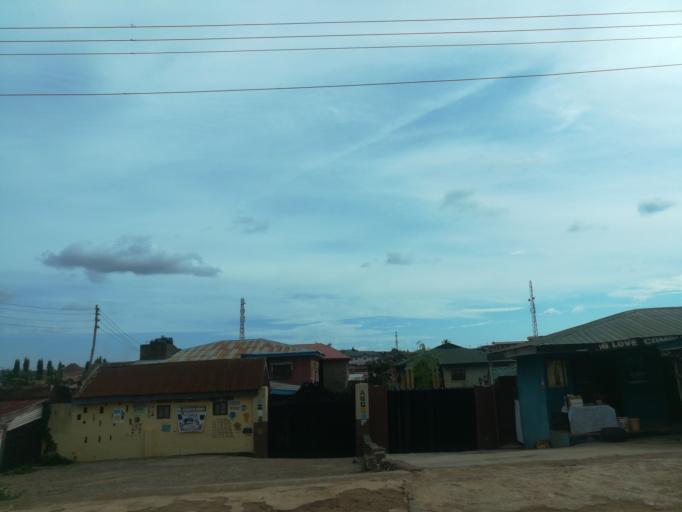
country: NG
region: Oyo
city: Ibadan
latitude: 7.3777
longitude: 3.9530
